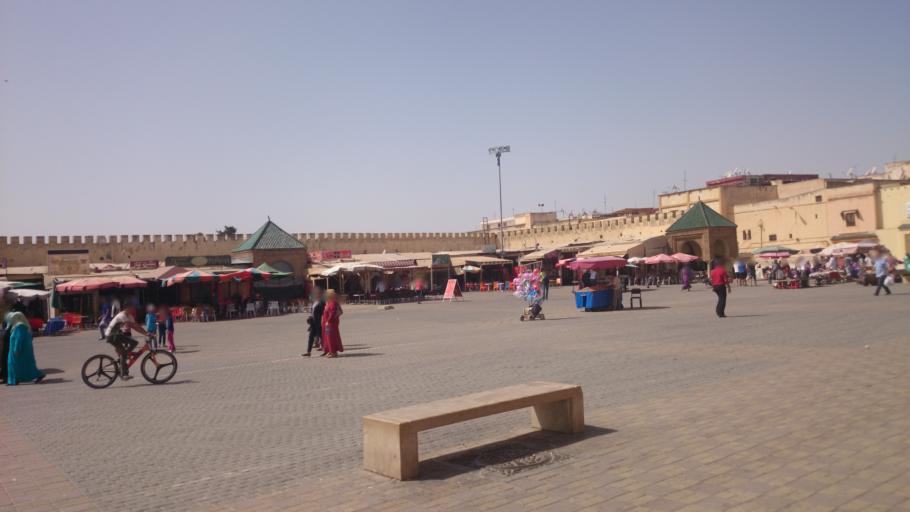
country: MA
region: Meknes-Tafilalet
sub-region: Meknes
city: Meknes
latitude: 33.8934
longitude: -5.5657
